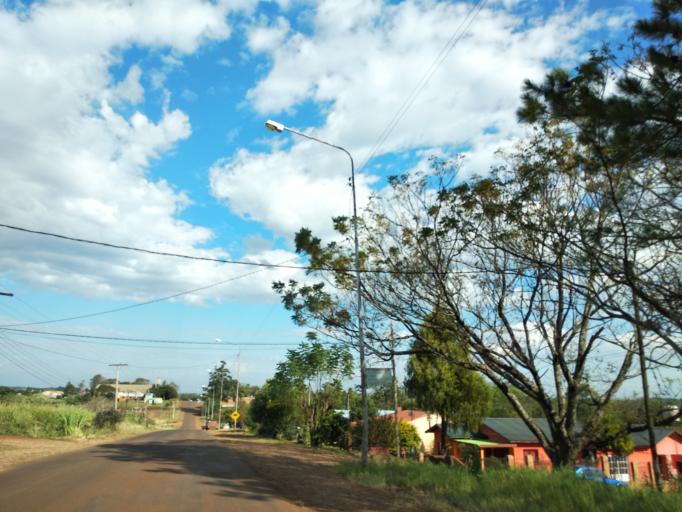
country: AR
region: Misiones
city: Aristobulo del Valle
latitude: -27.0798
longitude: -54.8316
